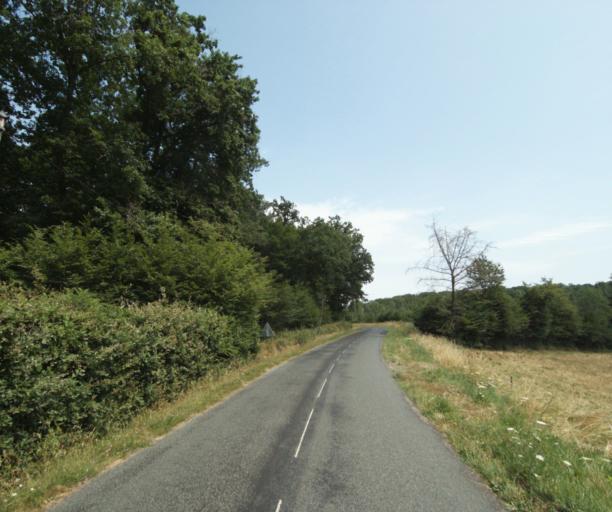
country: FR
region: Bourgogne
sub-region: Departement de Saone-et-Loire
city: Gueugnon
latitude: 46.5907
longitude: 4.0812
